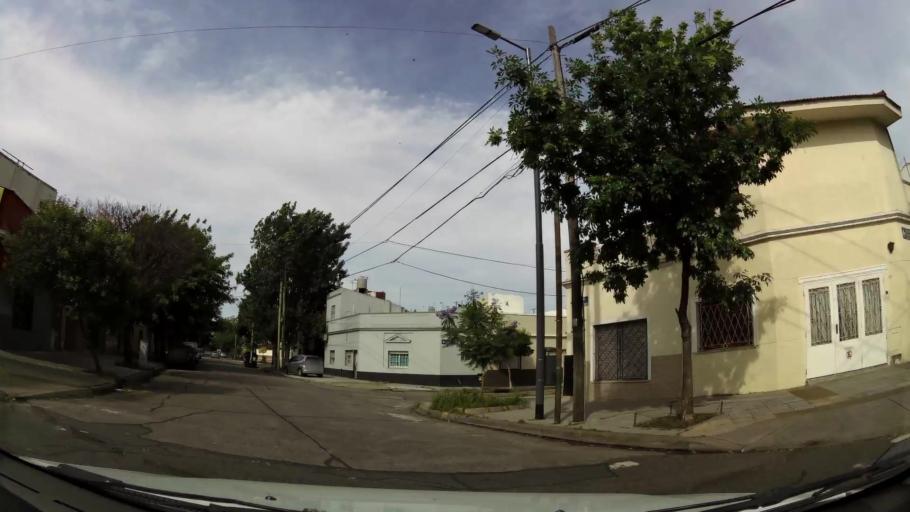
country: AR
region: Buenos Aires F.D.
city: Villa Lugano
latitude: -34.6562
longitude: -58.4795
